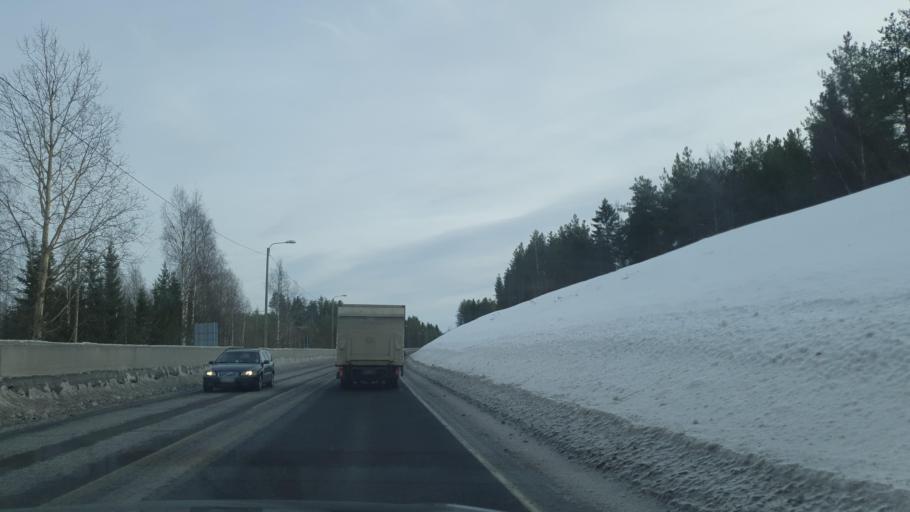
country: FI
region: Northern Ostrobothnia
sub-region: Oulu
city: Kempele
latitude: 64.9700
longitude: 25.6186
